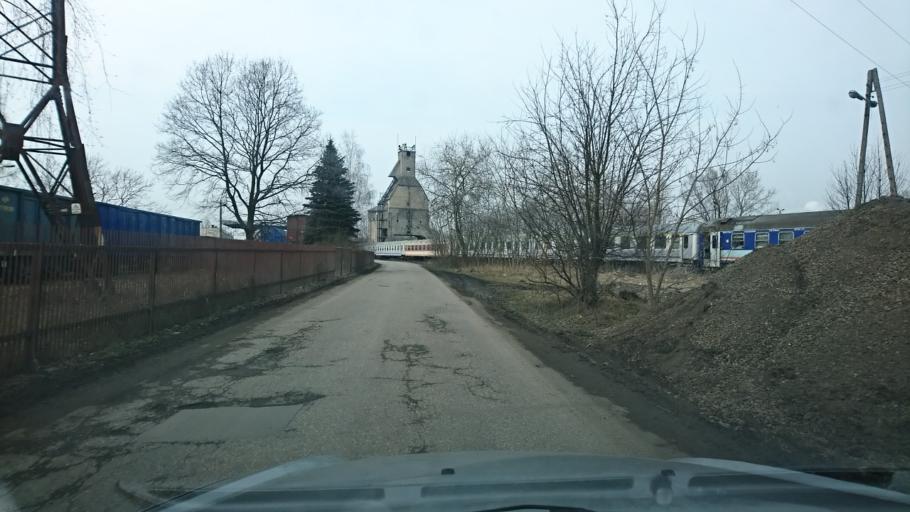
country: PL
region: Lesser Poland Voivodeship
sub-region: Powiat wielicki
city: Czarnochowice
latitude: 50.0238
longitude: 20.0261
